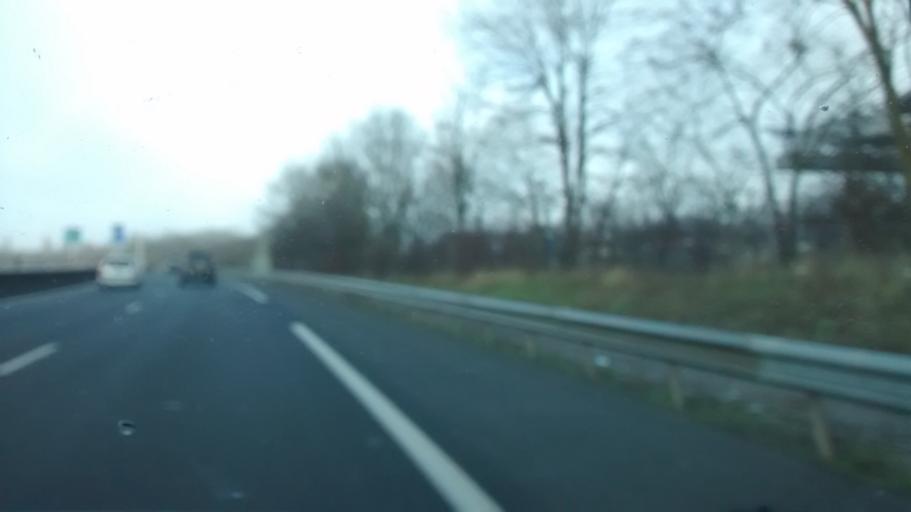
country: FR
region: Centre
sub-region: Departement d'Indre-et-Loire
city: Chambray-les-Tours
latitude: 47.3300
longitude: 0.6880
